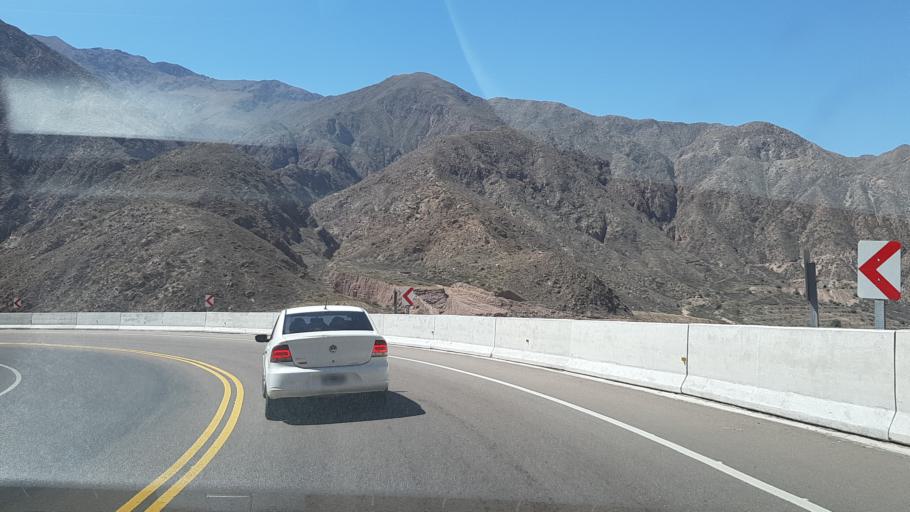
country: AR
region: Mendoza
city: Lujan de Cuyo
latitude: -33.0031
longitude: -69.1299
